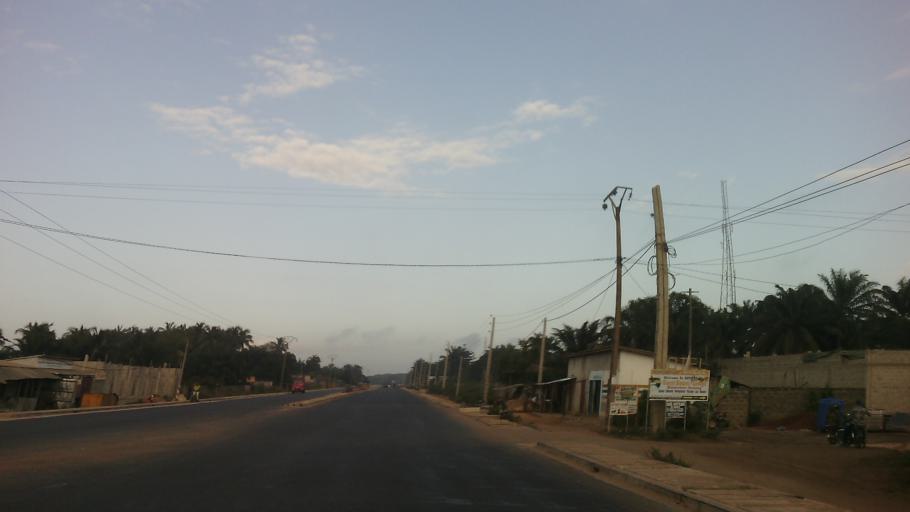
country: BJ
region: Atlantique
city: Hevie
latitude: 6.3828
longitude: 2.1805
